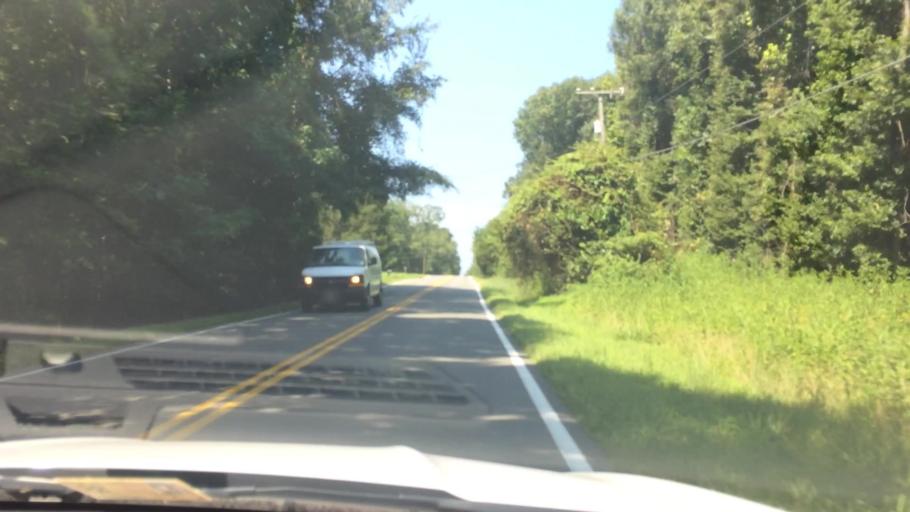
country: US
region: Virginia
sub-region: New Kent County
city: New Kent
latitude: 37.5265
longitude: -77.0321
